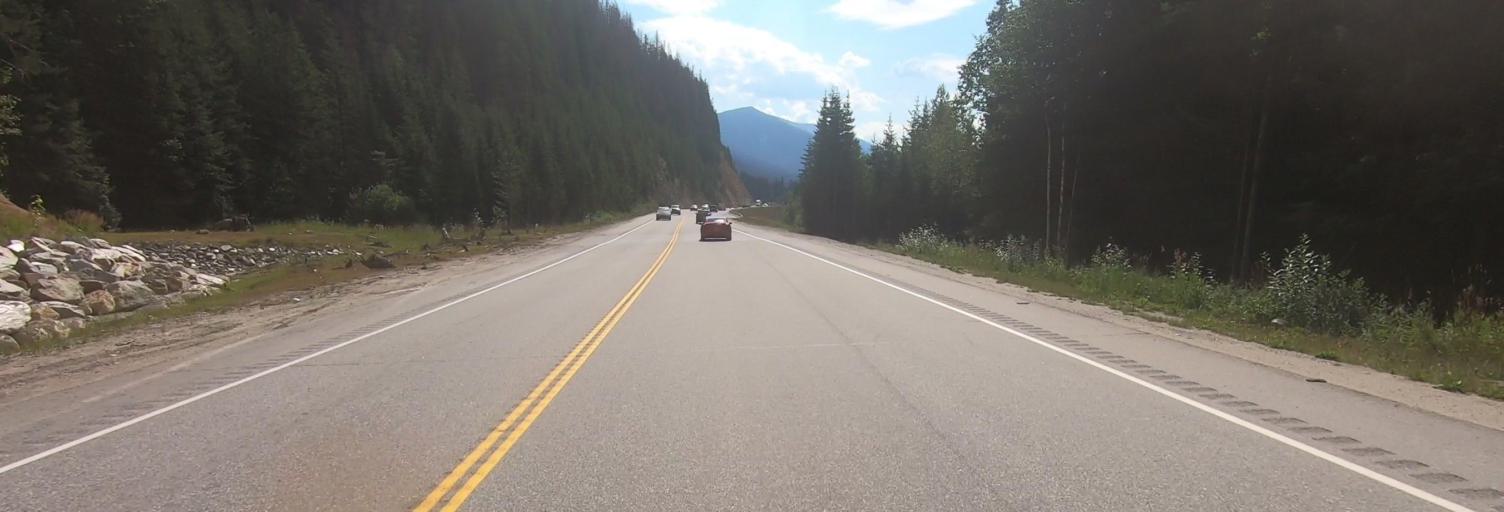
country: CA
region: British Columbia
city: Golden
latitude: 51.3954
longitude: -117.4585
